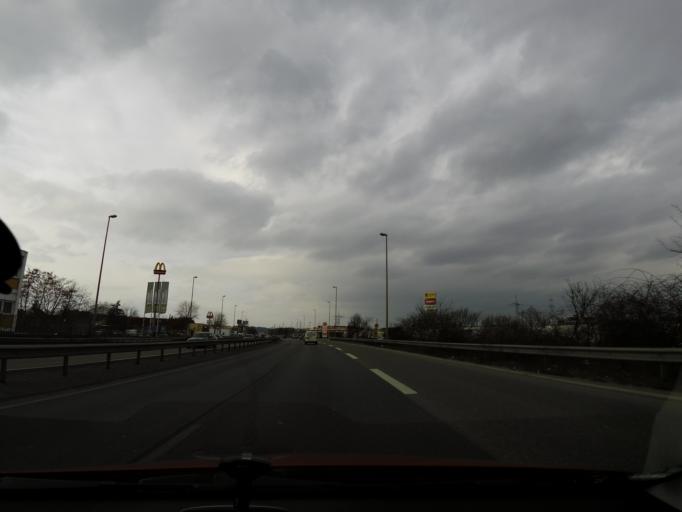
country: DE
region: Rheinland-Pfalz
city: Koblenz
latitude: 50.3796
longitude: 7.5805
